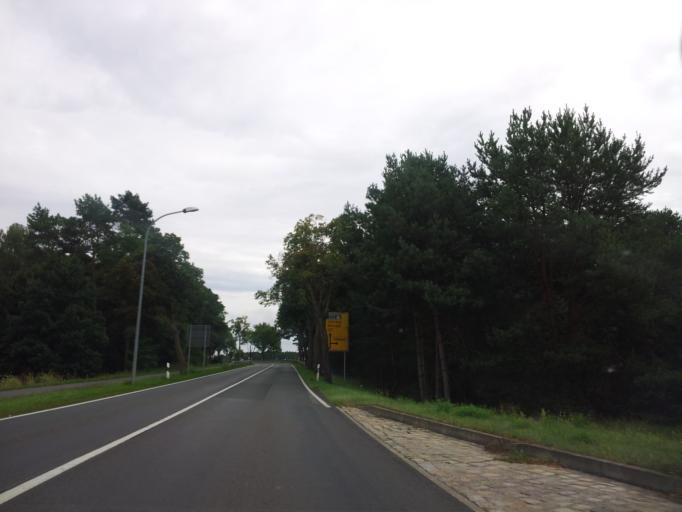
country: DE
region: Brandenburg
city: Belzig
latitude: 52.1301
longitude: 12.6298
